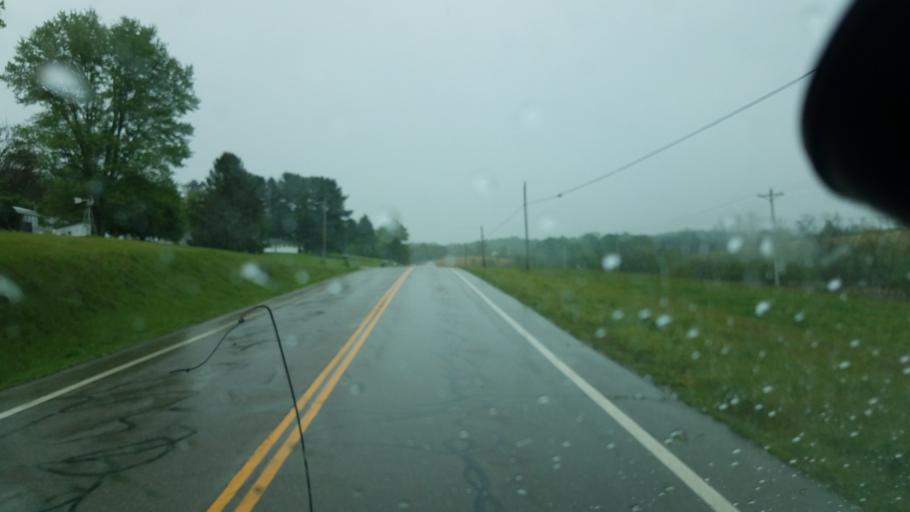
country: US
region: Ohio
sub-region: Muskingum County
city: Dresden
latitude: 40.0940
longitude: -82.0585
